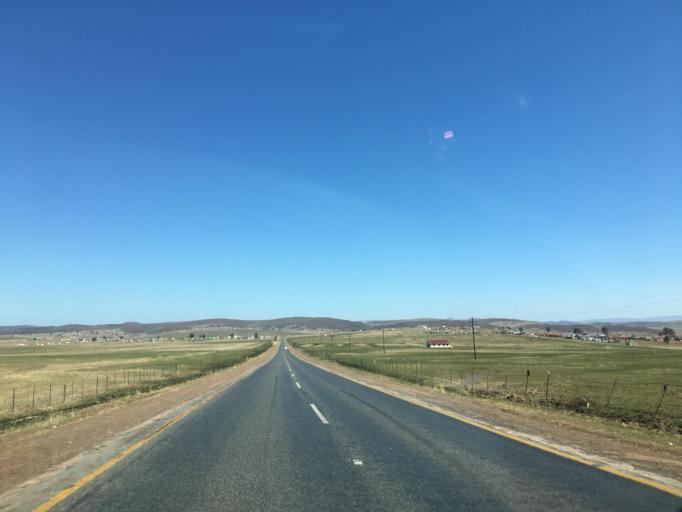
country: ZA
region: Eastern Cape
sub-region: Chris Hani District Municipality
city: Cofimvaba
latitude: -31.9445
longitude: 27.8349
